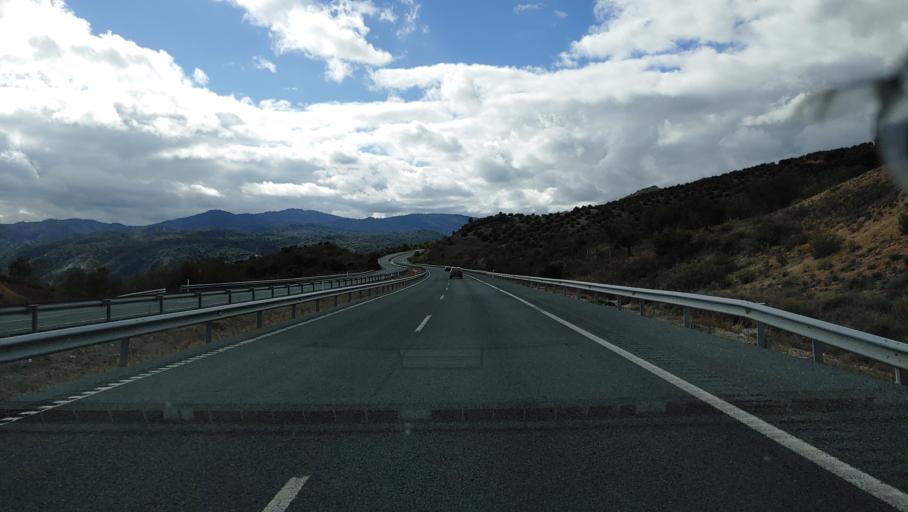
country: ES
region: Andalusia
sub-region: Provincia de Granada
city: Diezma
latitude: 37.3121
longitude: -3.3577
